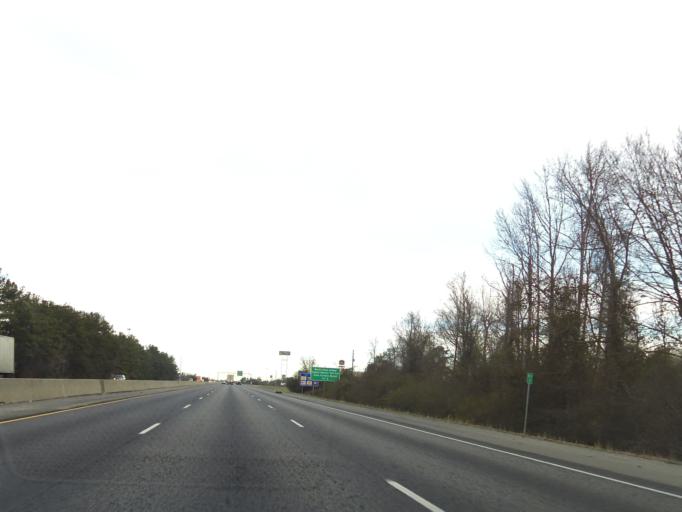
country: US
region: Georgia
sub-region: Bibb County
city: West Point
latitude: 32.8021
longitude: -83.7219
